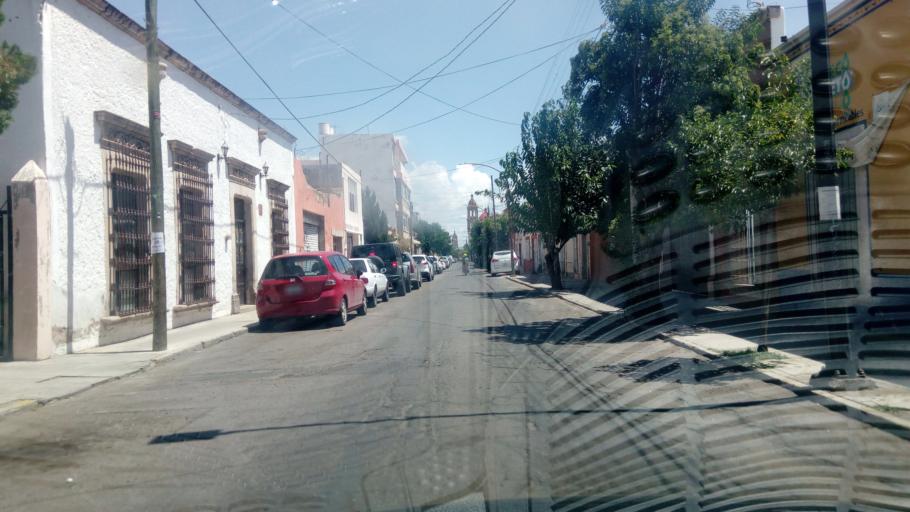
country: MX
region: Durango
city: Victoria de Durango
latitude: 24.0337
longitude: -104.6715
